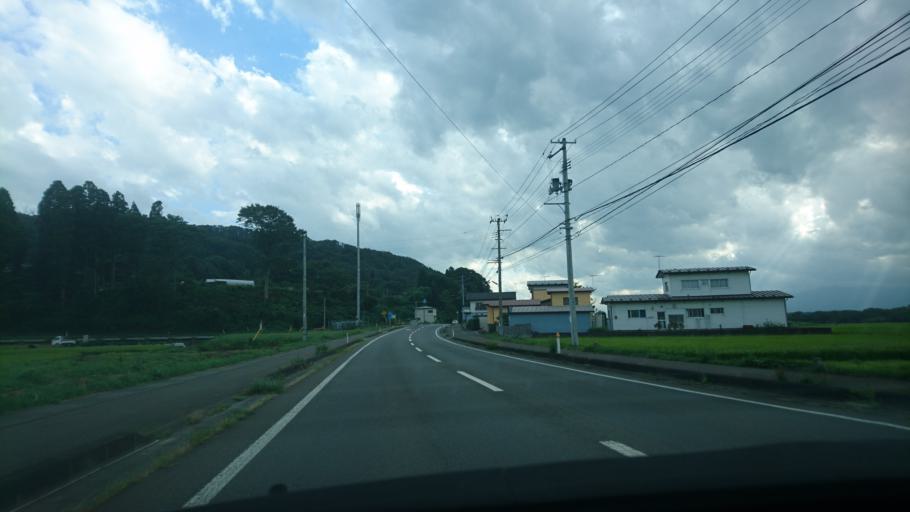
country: JP
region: Iwate
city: Kitakami
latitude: 39.2794
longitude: 141.1344
